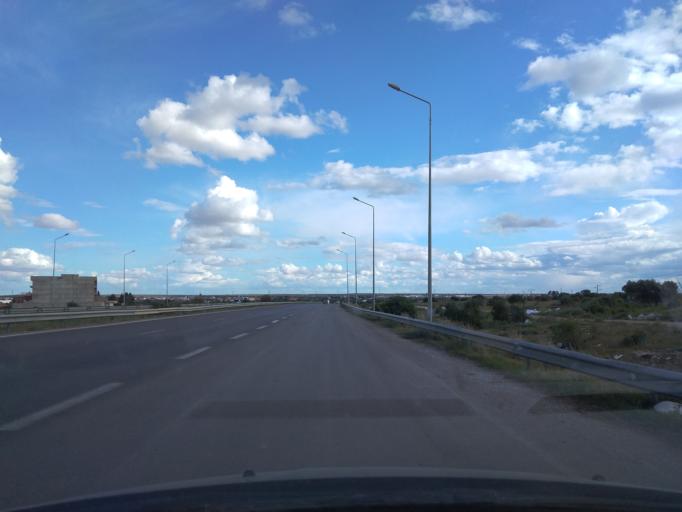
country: TN
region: Susah
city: Masakin
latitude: 35.7106
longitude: 10.5595
